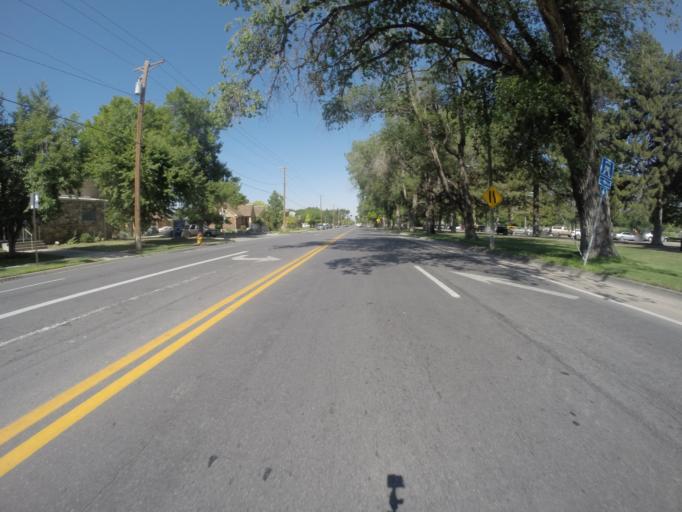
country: US
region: Utah
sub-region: Salt Lake County
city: Salt Lake City
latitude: 40.7418
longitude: -111.8716
